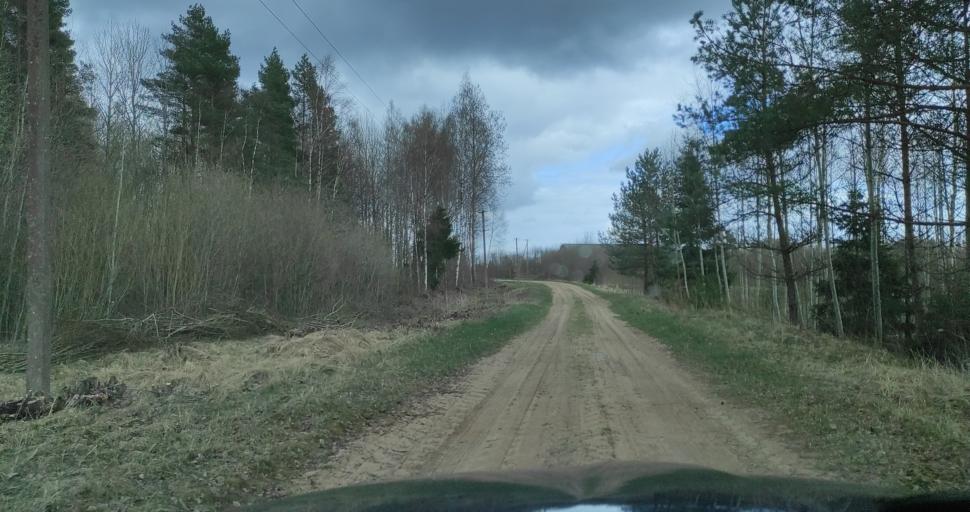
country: LV
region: Aizpute
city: Aizpute
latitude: 56.8256
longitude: 21.7690
